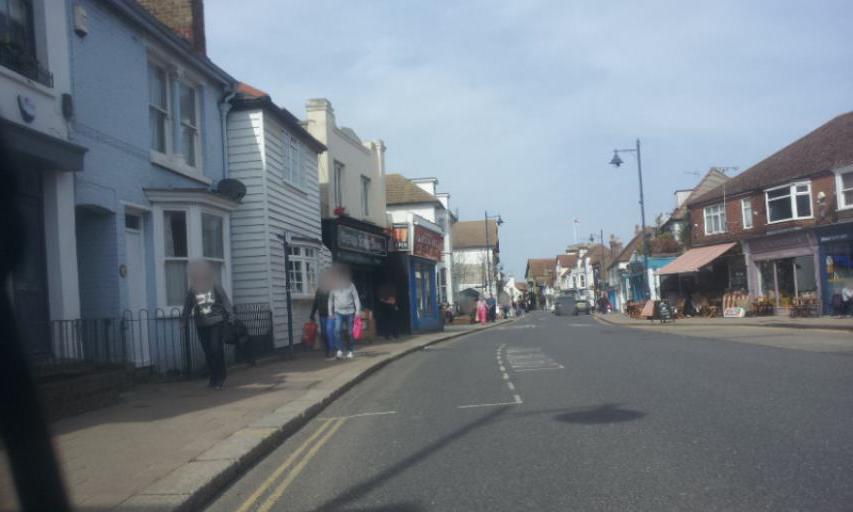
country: GB
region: England
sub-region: Kent
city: Whitstable
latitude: 51.3562
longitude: 1.0243
